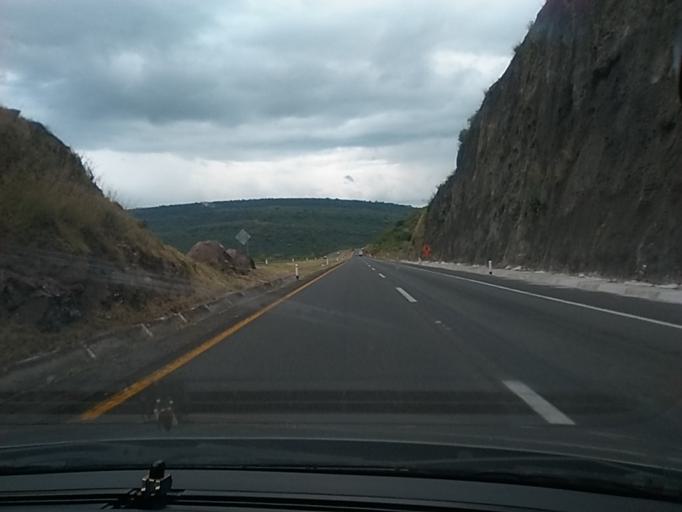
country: MX
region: Jalisco
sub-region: Zapotlan del Rey
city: Zapotlan del Rey
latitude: 20.5019
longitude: -102.9533
